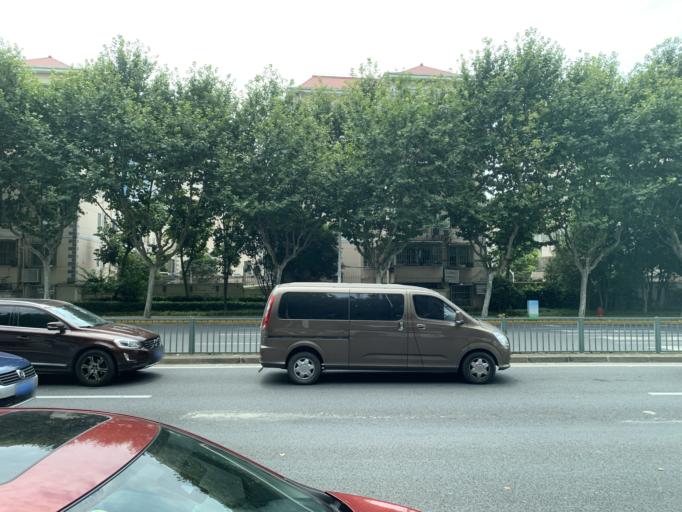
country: CN
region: Shanghai Shi
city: Pudong
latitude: 31.2345
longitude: 121.5194
